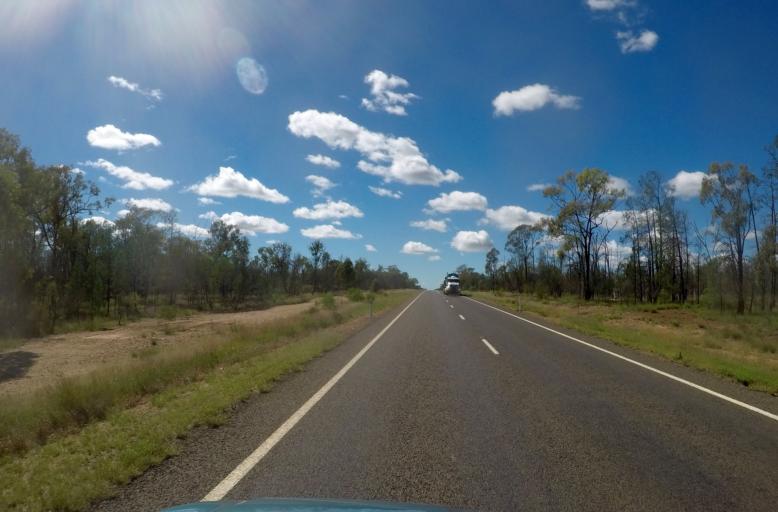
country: AU
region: Queensland
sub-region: Maranoa
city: Roma
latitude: -26.6211
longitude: 149.4548
